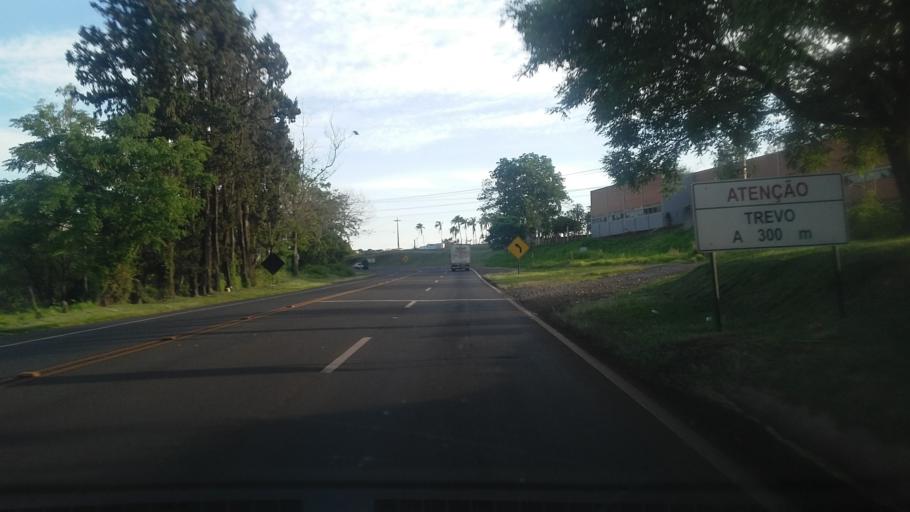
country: BR
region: Parana
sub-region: Assai
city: Assai
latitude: -23.2016
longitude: -50.6546
